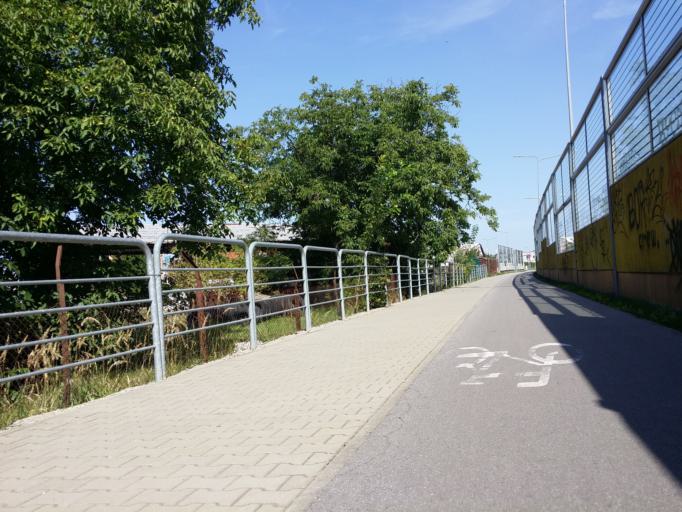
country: PL
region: Masovian Voivodeship
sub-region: Radom
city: Radom
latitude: 51.3790
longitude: 21.1698
